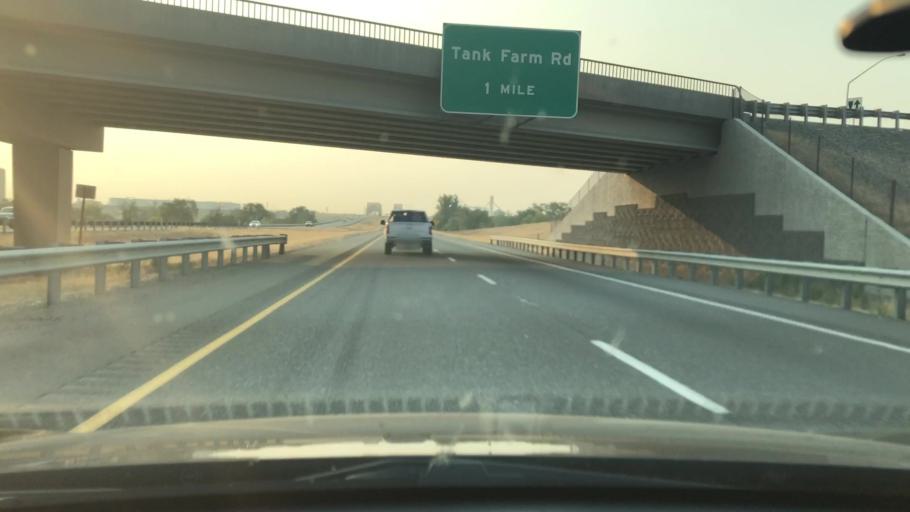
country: US
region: Washington
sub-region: Walla Walla County
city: Burbank
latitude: 46.2087
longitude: -119.0120
